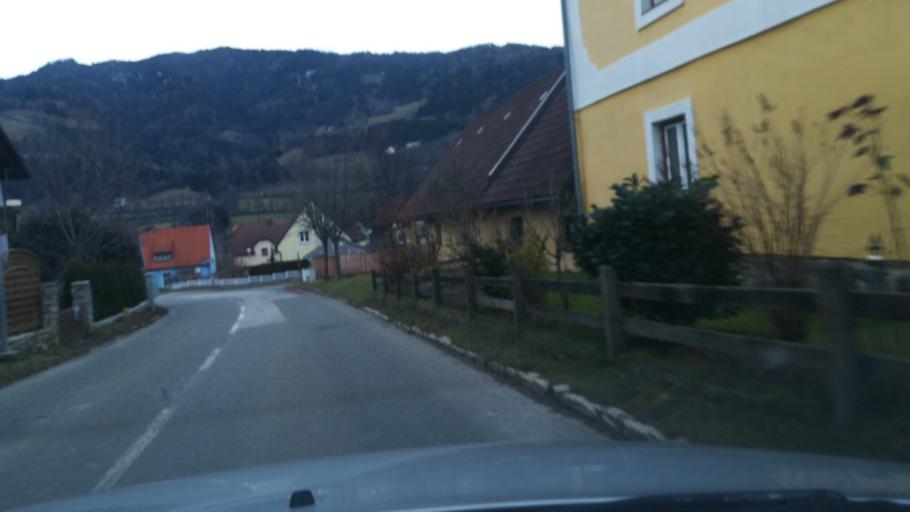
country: AT
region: Styria
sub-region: Politischer Bezirk Murtal
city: Sankt Georgen ob Judenburg
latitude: 47.2068
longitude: 14.4989
